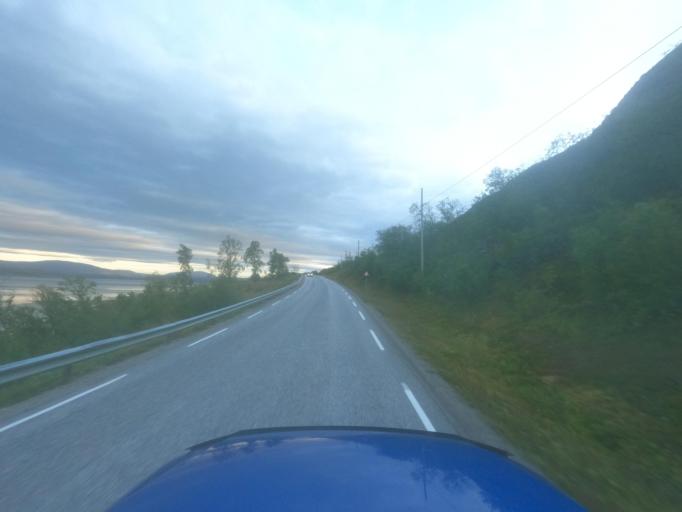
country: NO
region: Finnmark Fylke
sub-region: Porsanger
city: Lakselv
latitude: 70.1236
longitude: 24.9164
